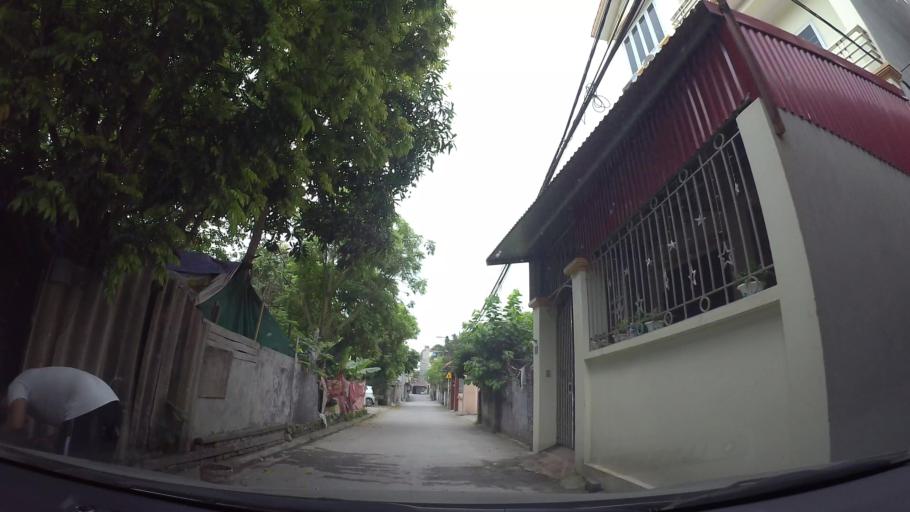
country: VN
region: Ha Noi
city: Trau Quy
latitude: 21.0599
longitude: 105.9190
